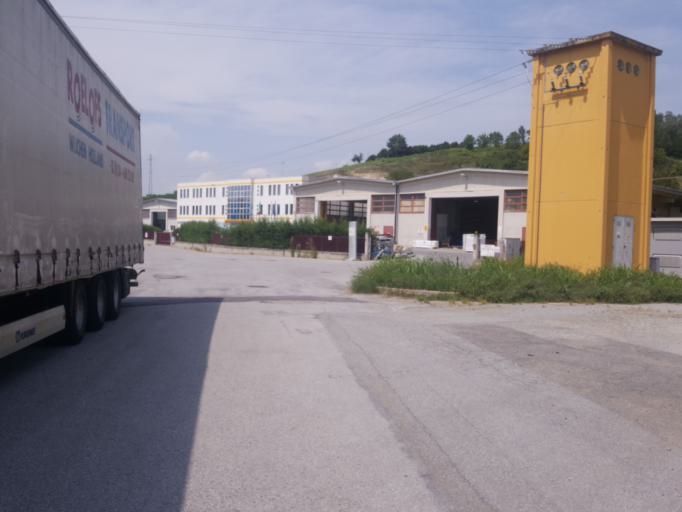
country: IT
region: Piedmont
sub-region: Provincia di Cuneo
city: Novello
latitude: 44.5933
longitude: 7.8976
